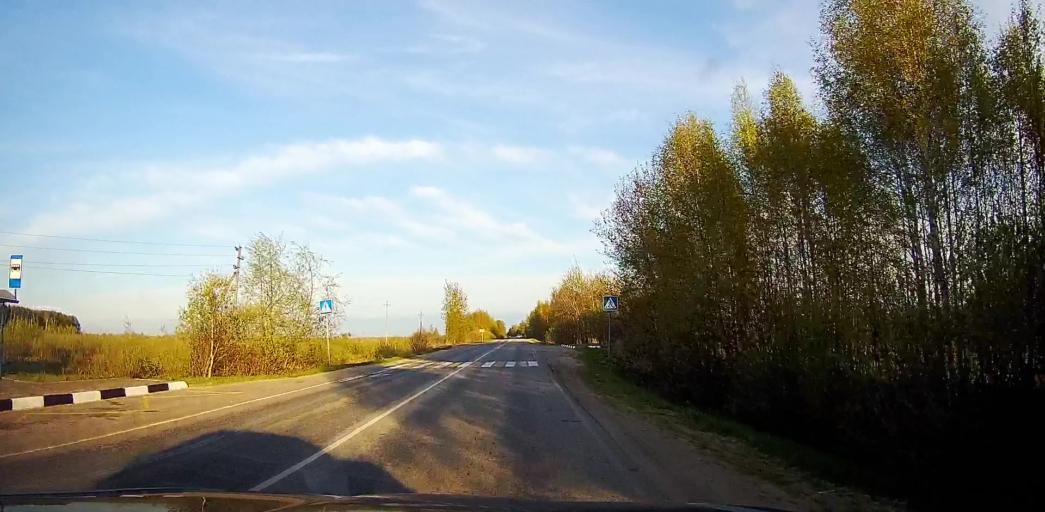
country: RU
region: Moskovskaya
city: Bronnitsy
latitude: 55.2781
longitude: 38.2200
